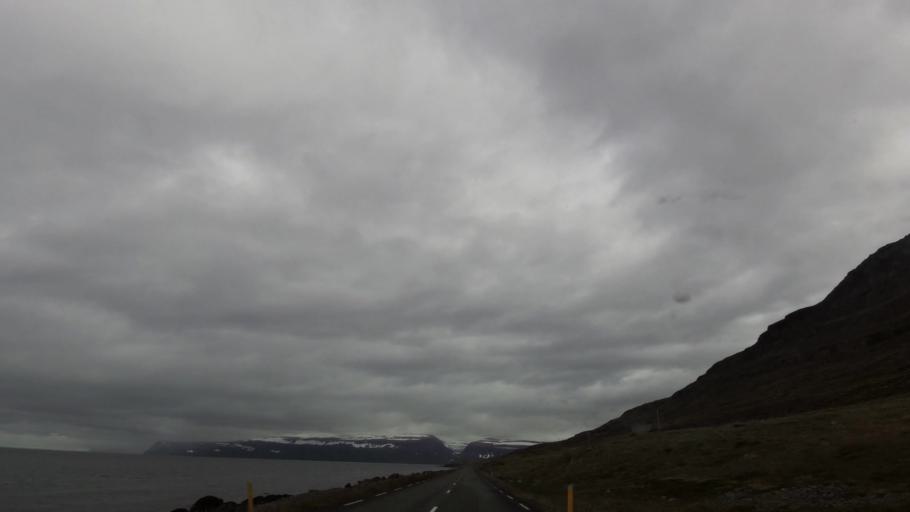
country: IS
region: Westfjords
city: Isafjoerdur
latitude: 66.0318
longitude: -22.7747
